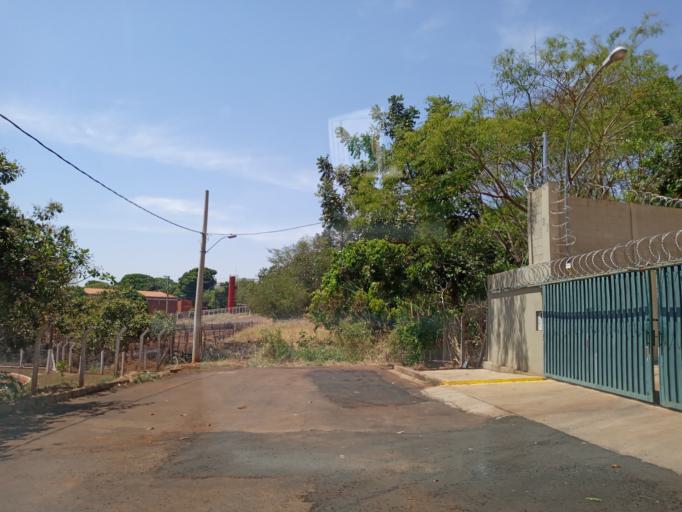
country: BR
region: Minas Gerais
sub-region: Ituiutaba
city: Ituiutaba
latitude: -18.9486
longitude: -49.4576
